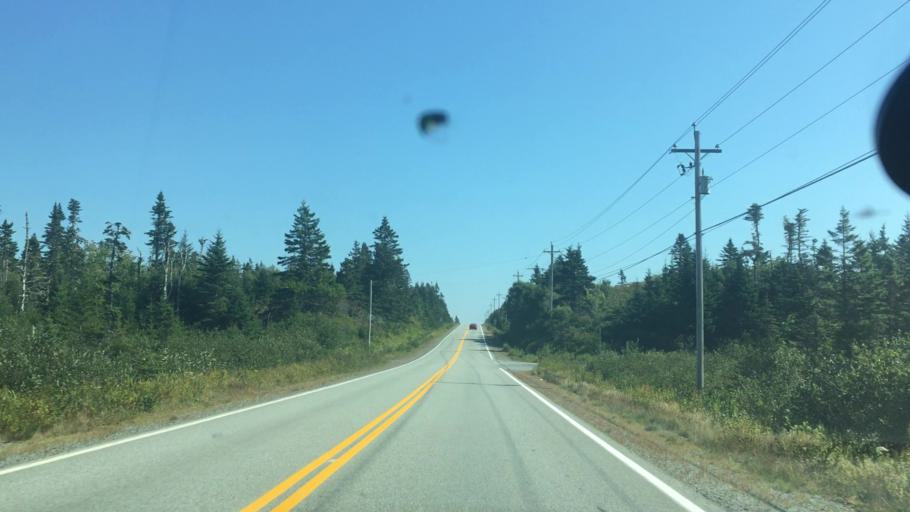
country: CA
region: Nova Scotia
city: New Glasgow
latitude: 44.9321
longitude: -62.2897
